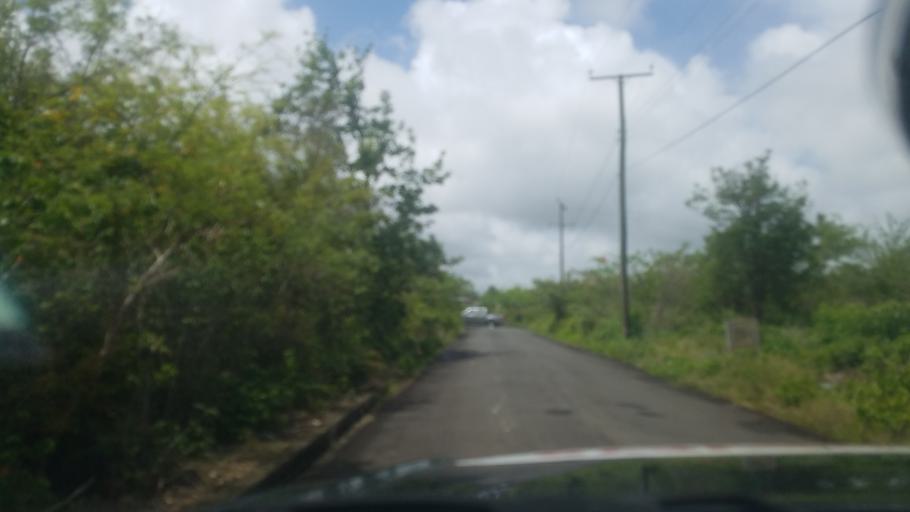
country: LC
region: Laborie Quarter
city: Laborie
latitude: 13.7394
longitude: -60.9756
